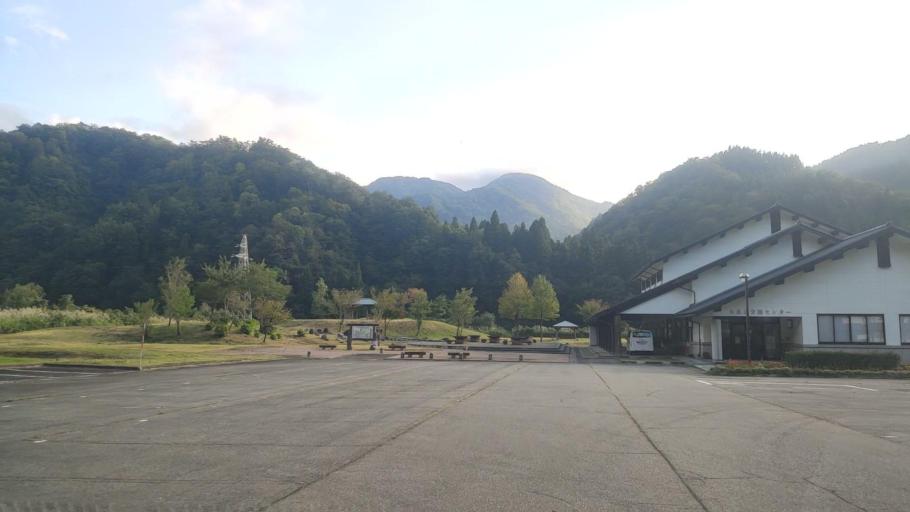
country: JP
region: Toyama
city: Yatsuomachi-higashikumisaka
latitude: 36.4797
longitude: 137.0810
